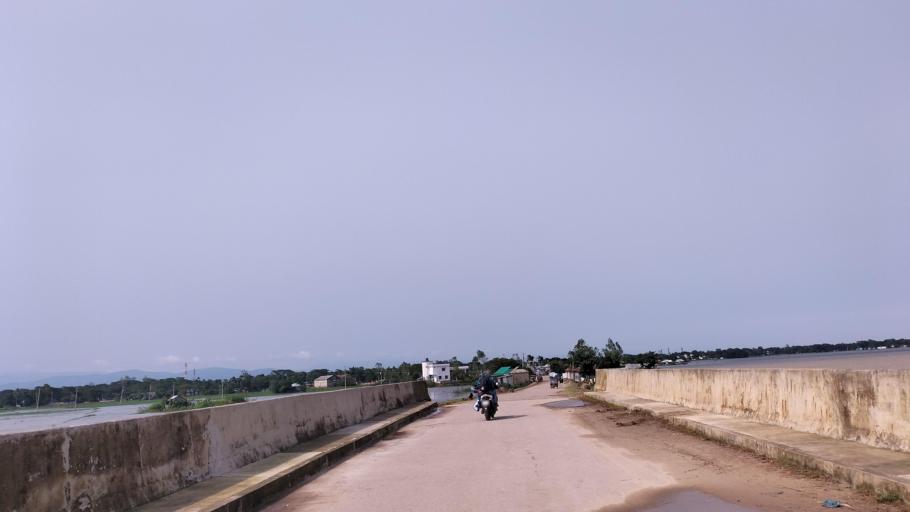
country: BD
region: Dhaka
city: Netrakona
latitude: 25.0674
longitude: 90.8822
